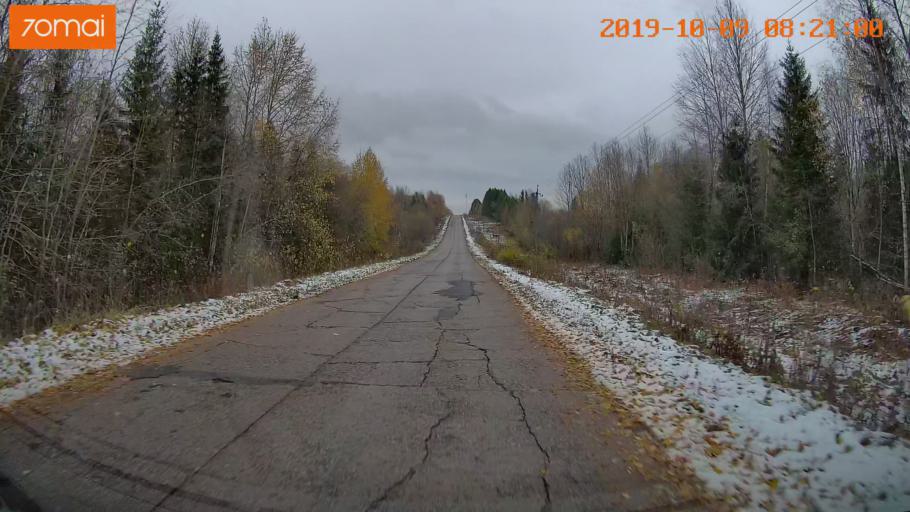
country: RU
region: Vologda
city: Gryazovets
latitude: 58.7424
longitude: 40.2691
